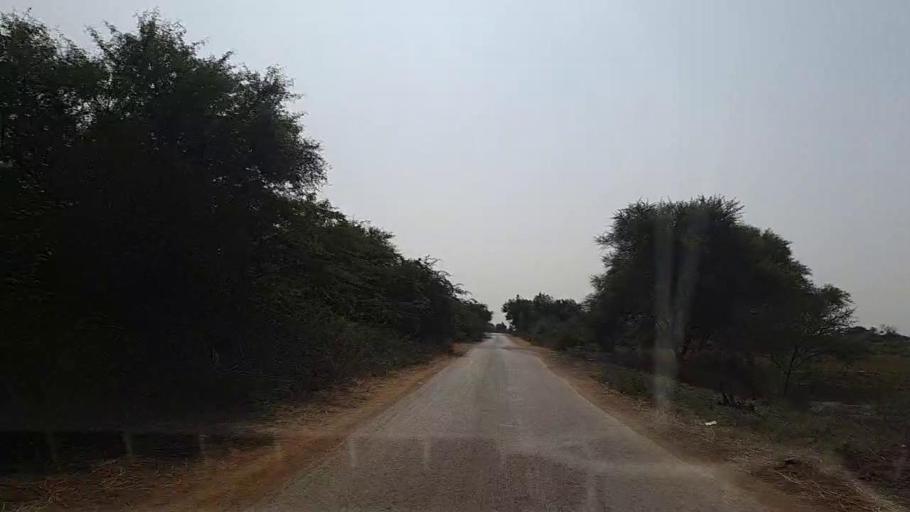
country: PK
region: Sindh
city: Chuhar Jamali
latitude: 24.2503
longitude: 67.9055
